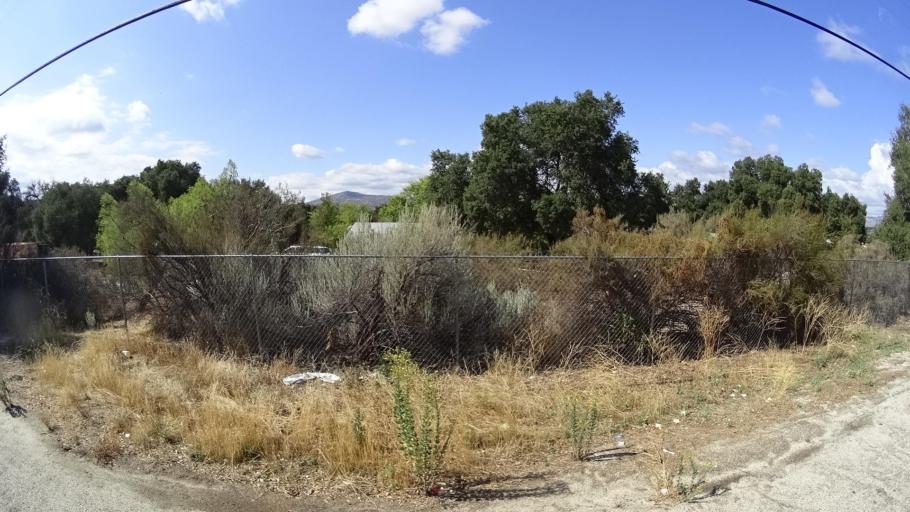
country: US
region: California
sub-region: San Diego County
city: Campo
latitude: 32.6765
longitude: -116.5059
